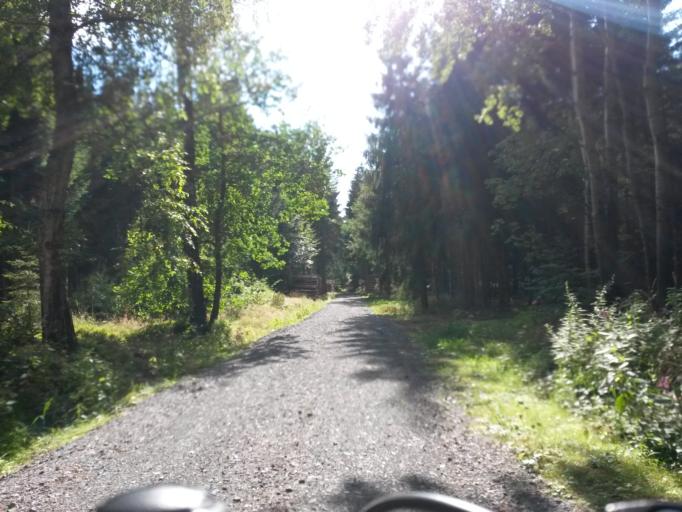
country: DE
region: Thuringia
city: Bad Klosterlausnitz
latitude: 50.9021
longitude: 11.8783
